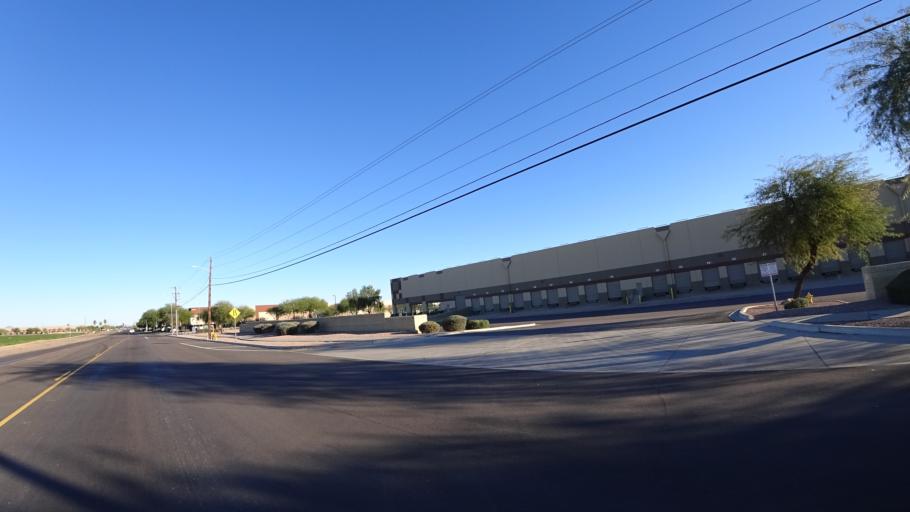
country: US
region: Arizona
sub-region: Maricopa County
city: Tolleson
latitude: 33.4501
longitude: -112.2817
